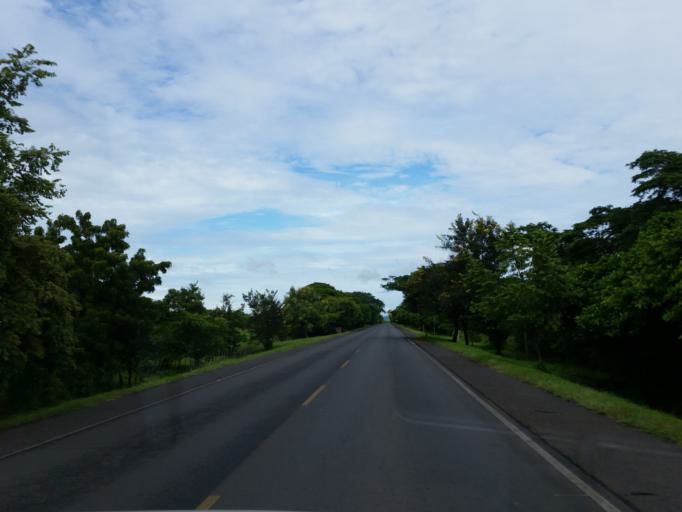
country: NI
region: Leon
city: Nagarote
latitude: 12.2967
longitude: -86.5929
